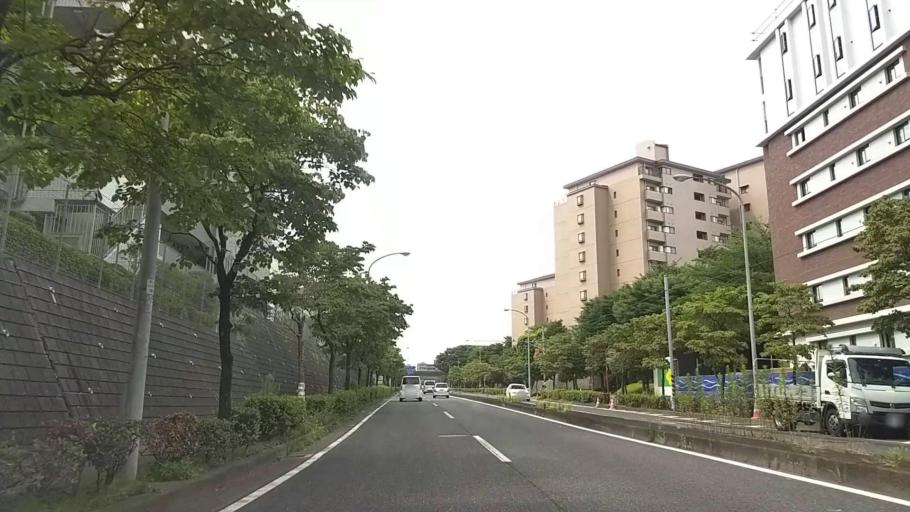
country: JP
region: Kanagawa
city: Yokohama
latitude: 35.5399
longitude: 139.5860
